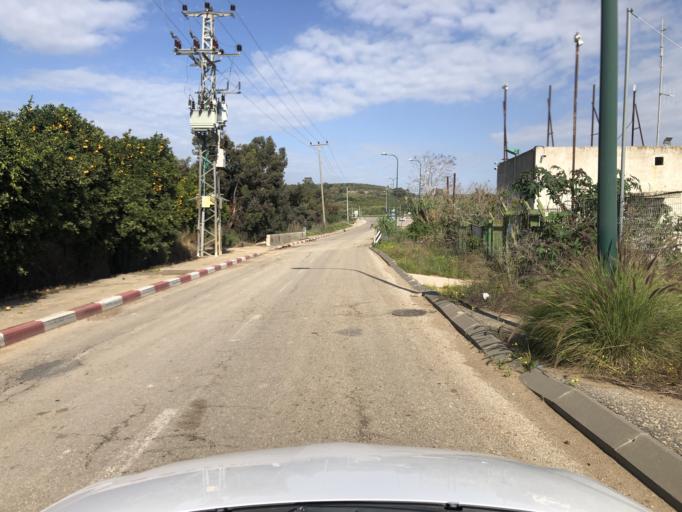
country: IL
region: Central District
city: Ness Ziona
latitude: 31.9187
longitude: 34.7787
